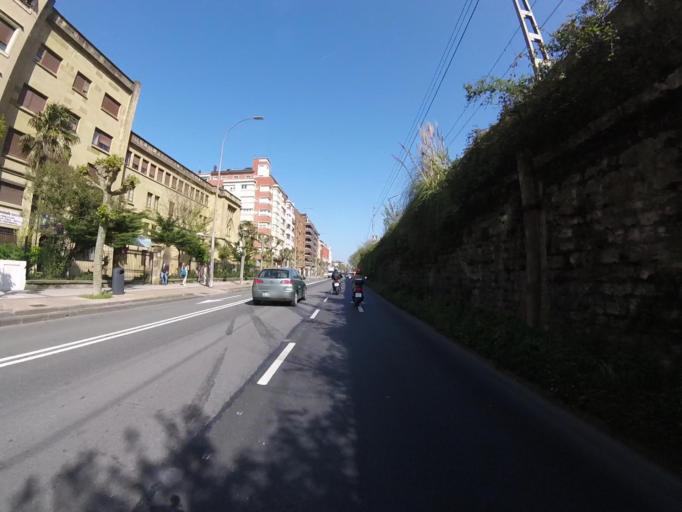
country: ES
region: Basque Country
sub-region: Provincia de Guipuzcoa
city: San Sebastian
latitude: 43.3223
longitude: -1.9707
